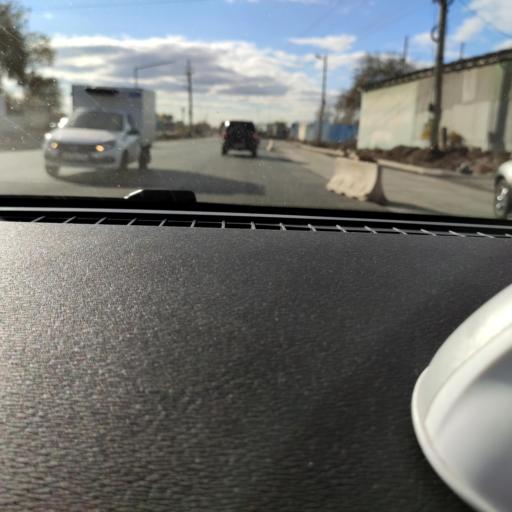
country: RU
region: Samara
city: Samara
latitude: 53.1825
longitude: 50.2142
